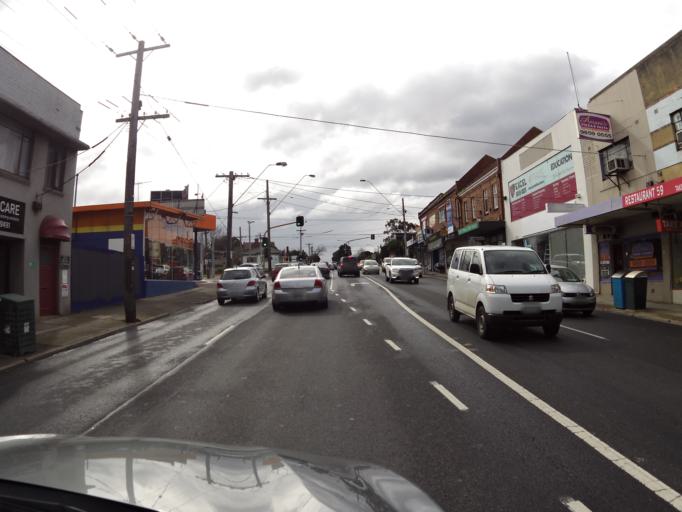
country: AU
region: Victoria
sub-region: Boroondara
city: Kew East
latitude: -37.7941
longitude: 145.0638
